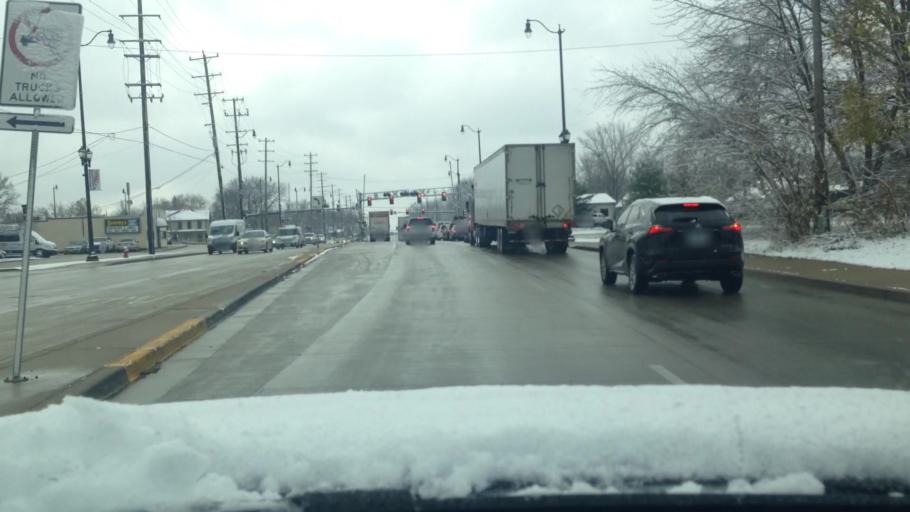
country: US
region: Illinois
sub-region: McHenry County
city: Huntley
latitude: 42.1702
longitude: -88.4280
